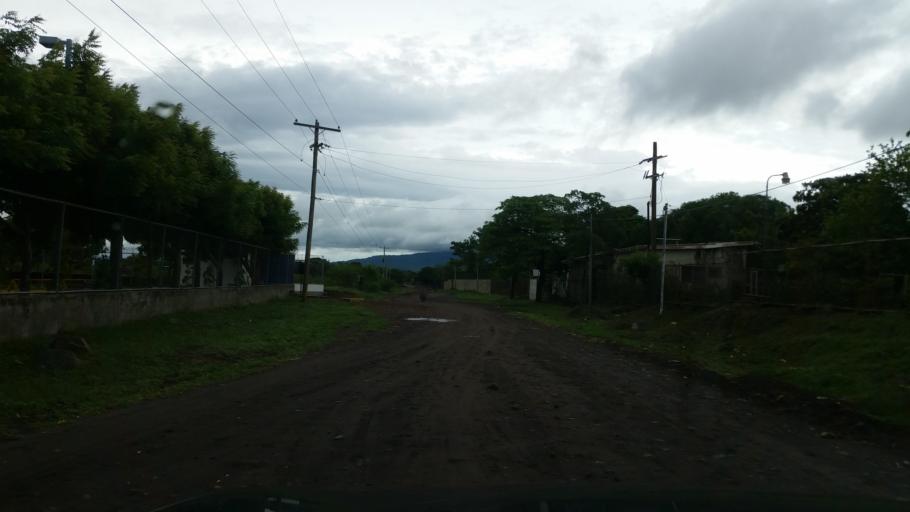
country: NI
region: Granada
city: Granada
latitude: 11.9510
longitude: -85.9537
